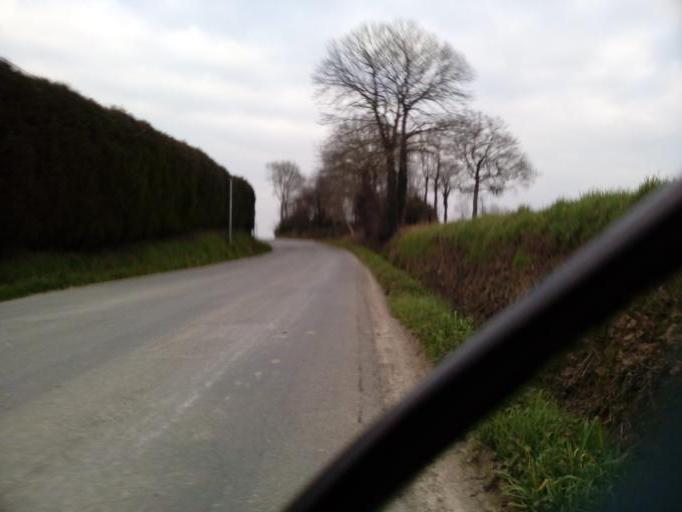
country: FR
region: Brittany
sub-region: Departement d'Ille-et-Vilaine
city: Talensac
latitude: 48.1046
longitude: -1.9044
